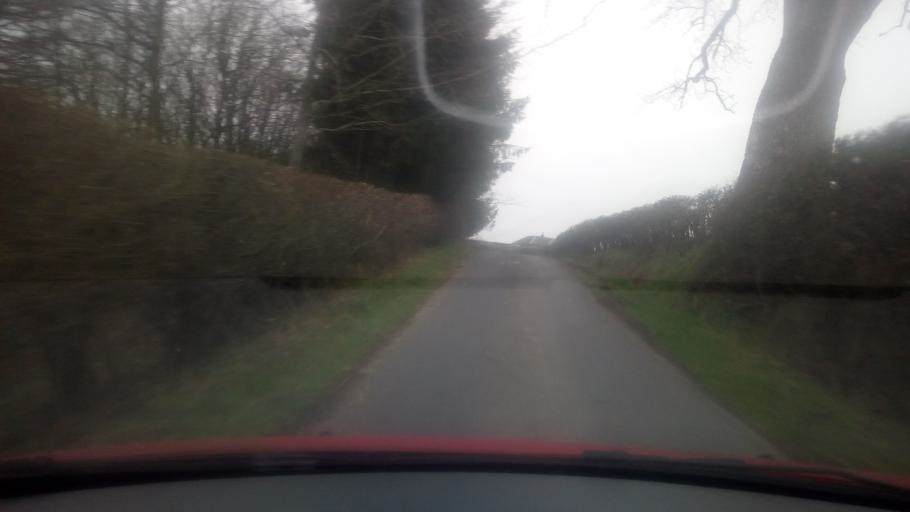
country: GB
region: Scotland
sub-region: The Scottish Borders
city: Hawick
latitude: 55.4394
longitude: -2.6910
